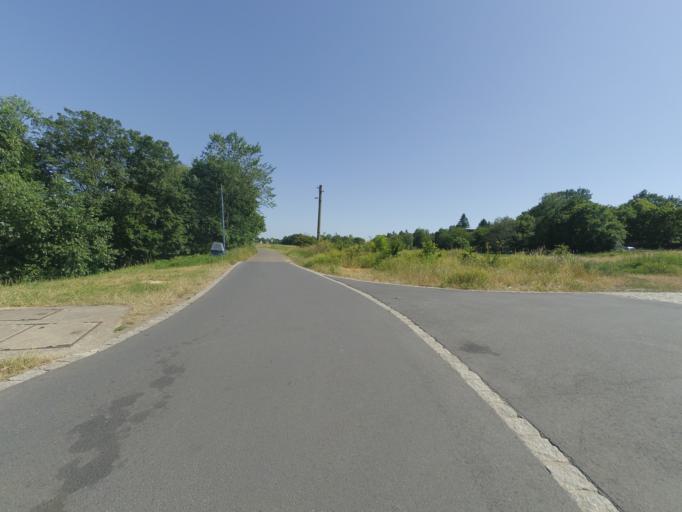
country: DE
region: Saxony
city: Albertstadt
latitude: 51.0399
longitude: 13.8196
